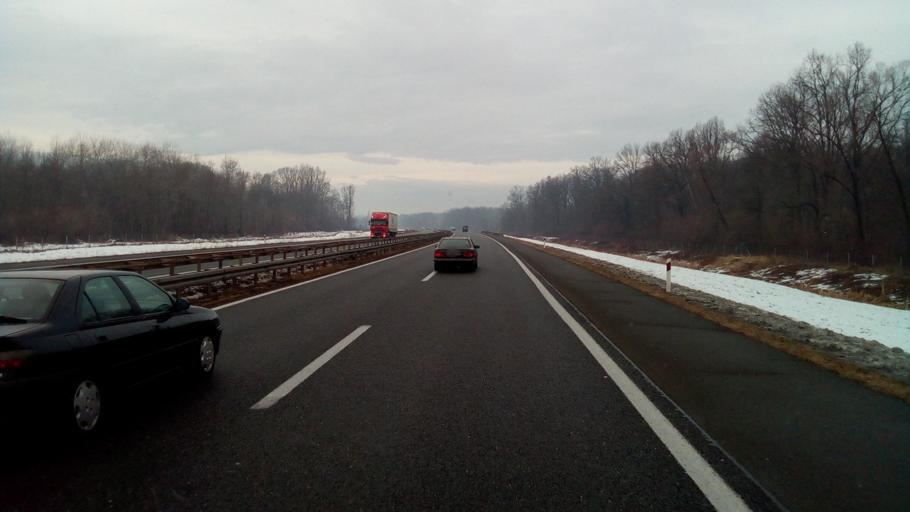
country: HR
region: Zagrebacka
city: Lupoglav
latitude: 45.7362
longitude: 16.3330
